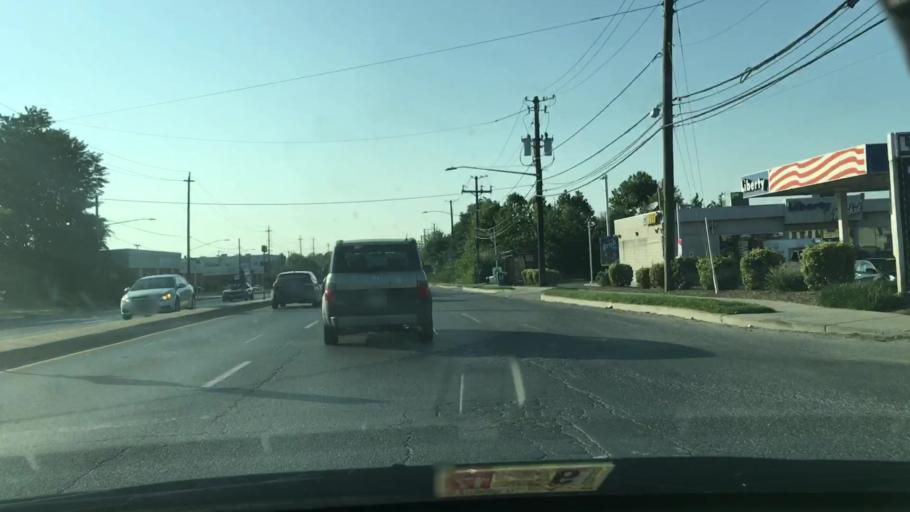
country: US
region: Maryland
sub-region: Montgomery County
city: Rockville
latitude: 39.0979
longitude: -77.1366
